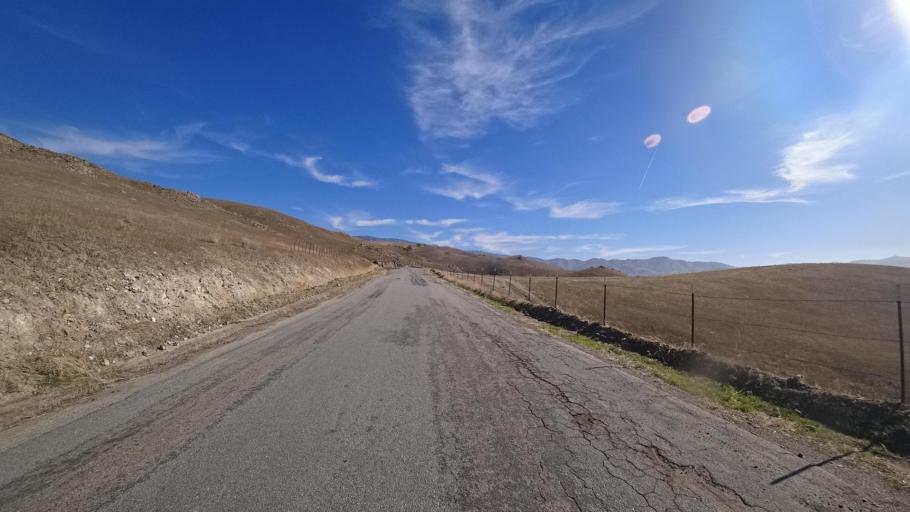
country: US
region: California
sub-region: Kern County
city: Arvin
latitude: 35.4113
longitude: -118.7502
